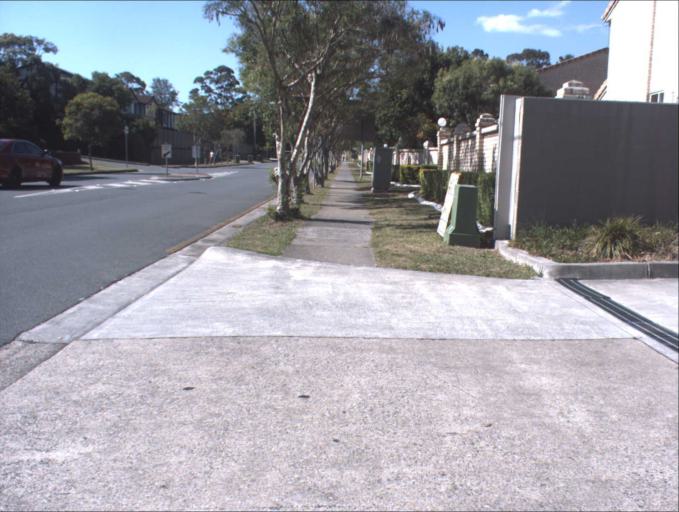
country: AU
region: Queensland
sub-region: Logan
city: Slacks Creek
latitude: -27.6332
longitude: 153.1389
